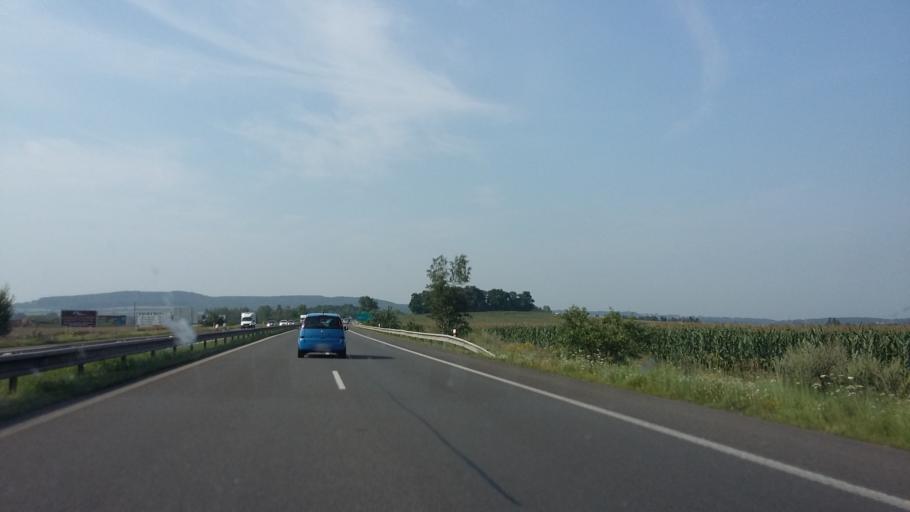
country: CZ
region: Central Bohemia
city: Bakov nad Jizerou
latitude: 50.4884
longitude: 14.9705
